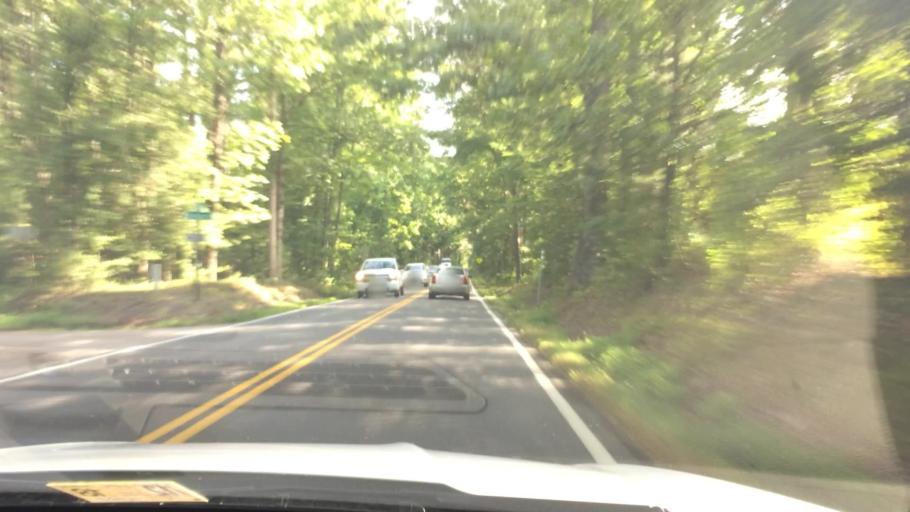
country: US
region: Virginia
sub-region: King William County
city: West Point
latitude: 37.4626
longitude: -76.8392
